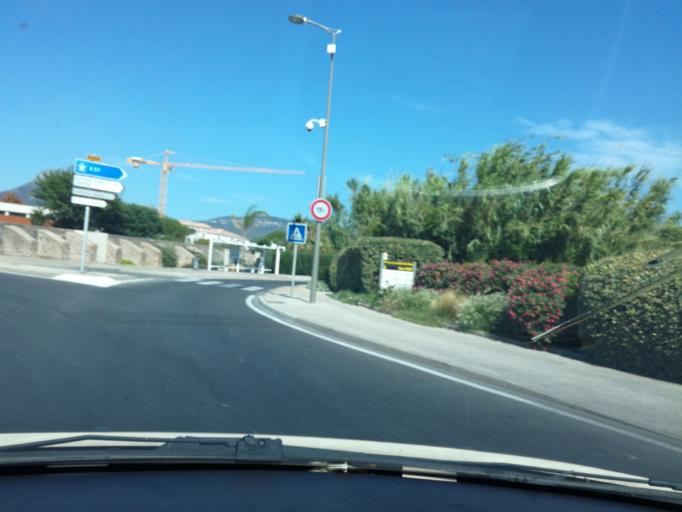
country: FR
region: Provence-Alpes-Cote d'Azur
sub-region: Departement du Var
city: La Crau
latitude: 43.1444
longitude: 6.0795
